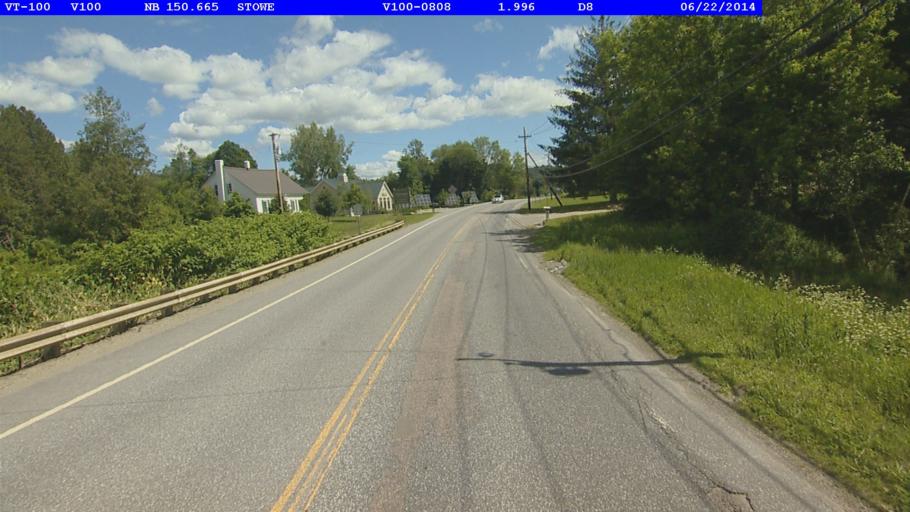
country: US
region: Vermont
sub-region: Washington County
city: Waterbury
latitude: 44.4491
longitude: -72.6993
